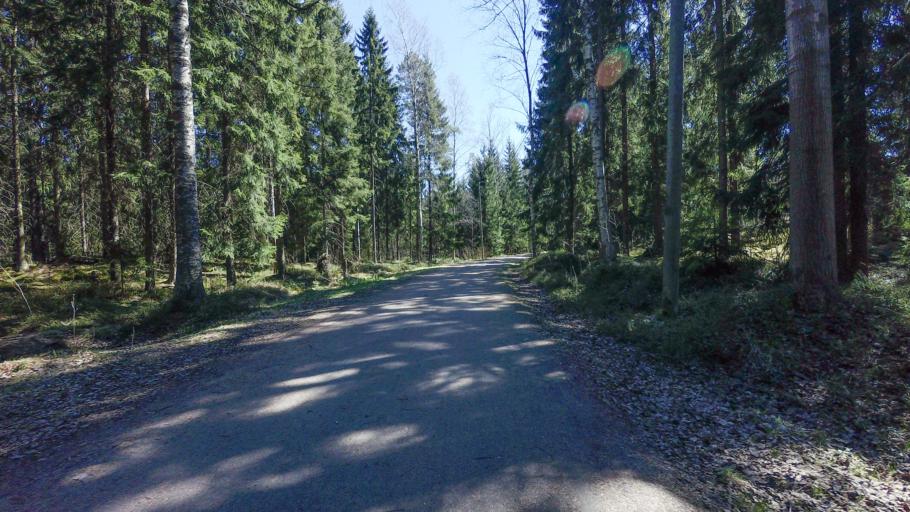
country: FI
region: Uusimaa
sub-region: Helsinki
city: Vantaa
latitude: 60.2302
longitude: 25.1454
